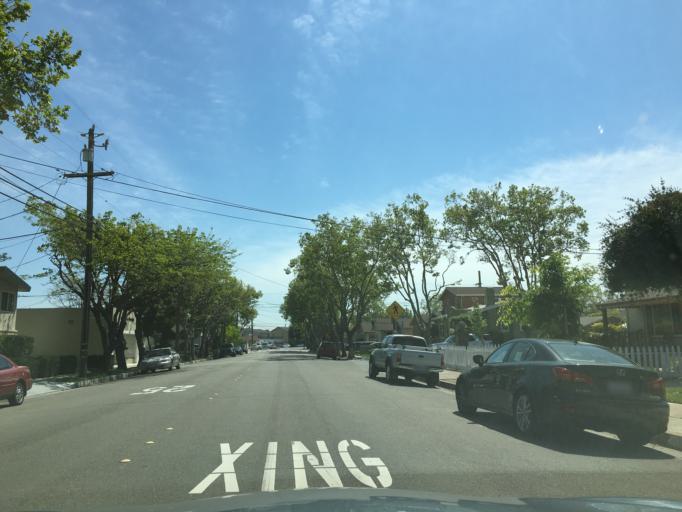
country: US
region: California
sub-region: San Mateo County
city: San Mateo
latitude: 37.5569
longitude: -122.3127
